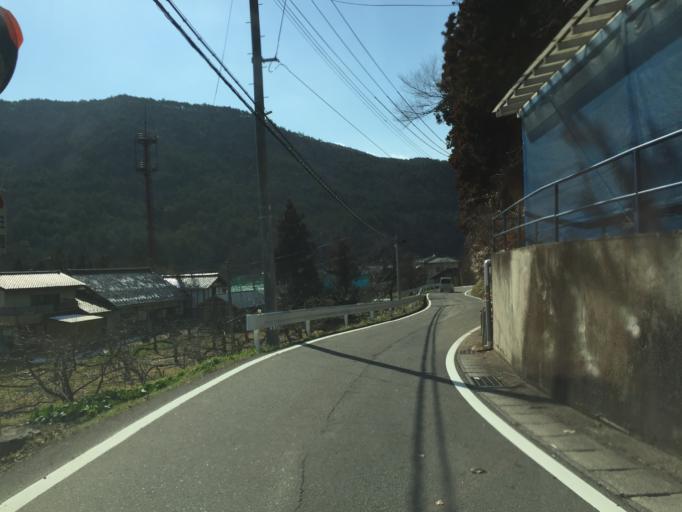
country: JP
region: Fukushima
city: Fukushima-shi
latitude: 37.8255
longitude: 140.4139
